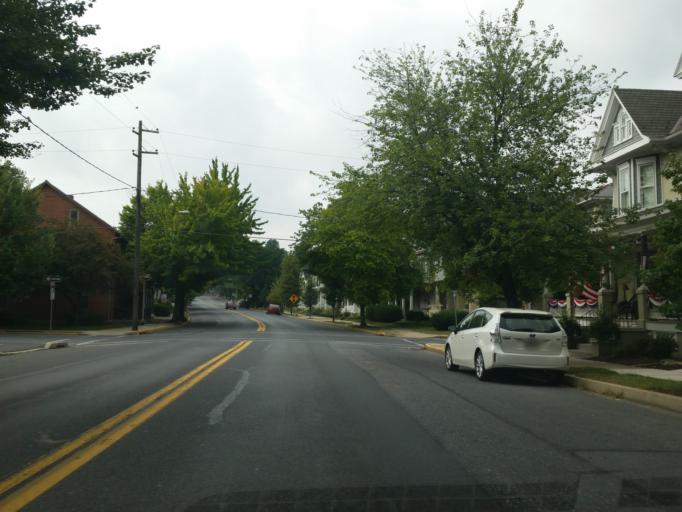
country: US
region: Pennsylvania
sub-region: Lancaster County
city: Lititz
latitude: 40.1521
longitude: -76.3072
